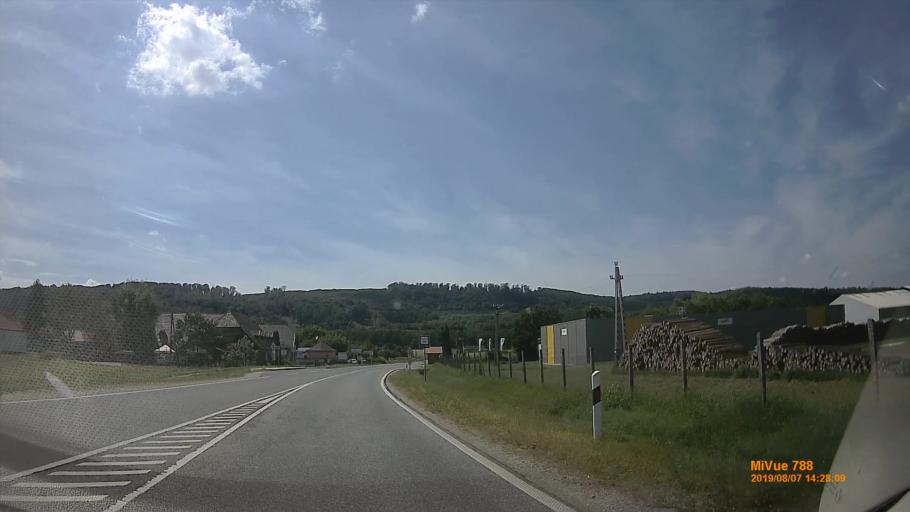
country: HU
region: Zala
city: Zalaegerszeg
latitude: 46.8270
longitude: 16.9380
